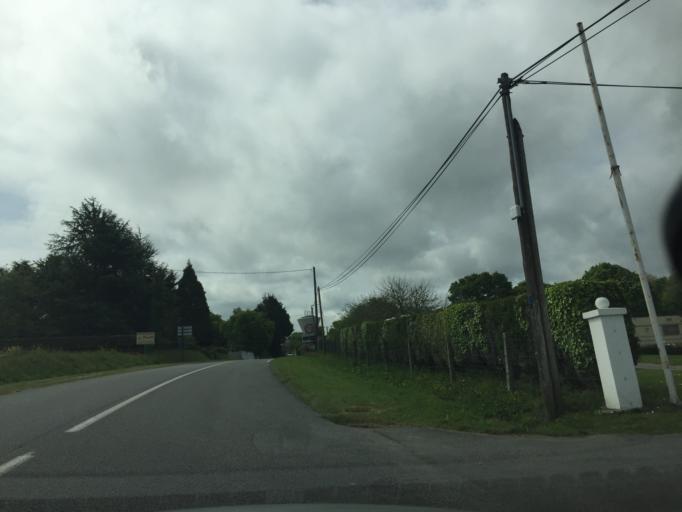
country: FR
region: Brittany
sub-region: Departement des Cotes-d'Armor
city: Saint-Cast-le-Guildo
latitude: 48.6040
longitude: -2.2415
